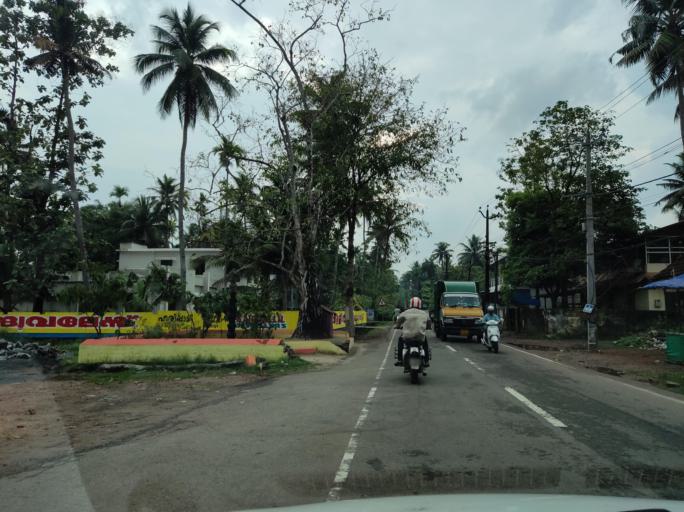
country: IN
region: Kerala
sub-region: Alappuzha
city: Kayankulam
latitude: 9.2594
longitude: 76.4404
